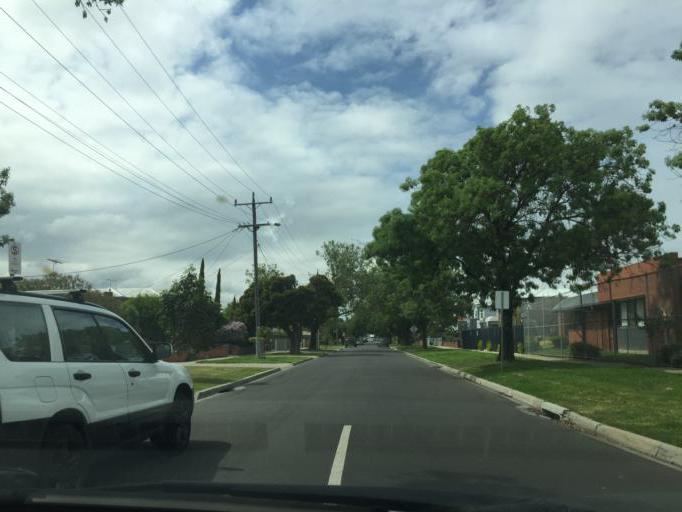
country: AU
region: Victoria
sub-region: Hobsons Bay
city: South Kingsville
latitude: -37.8288
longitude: 144.8777
